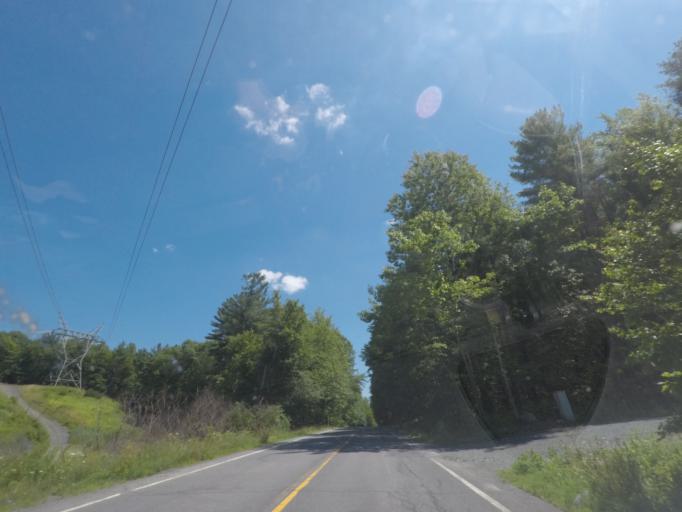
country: US
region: New York
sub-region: Rensselaer County
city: Averill Park
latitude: 42.5843
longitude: -73.5158
